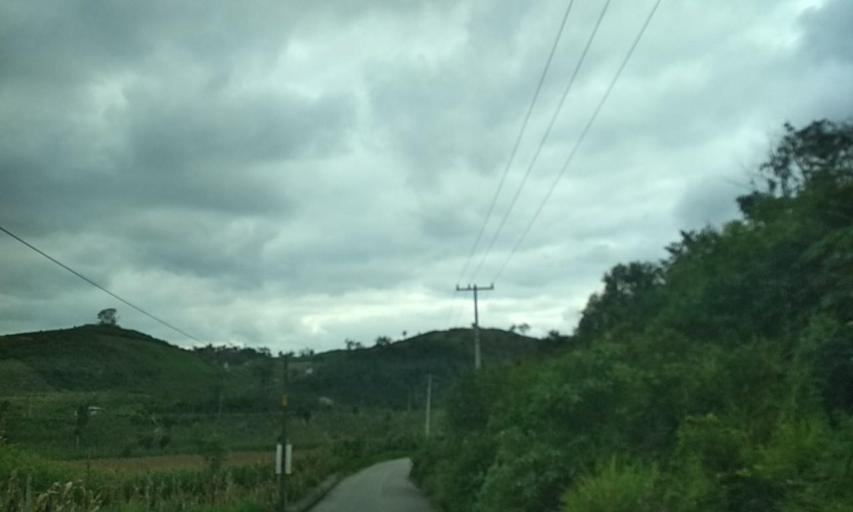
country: MX
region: Veracruz
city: Papantla de Olarte
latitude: 20.4717
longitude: -97.3202
